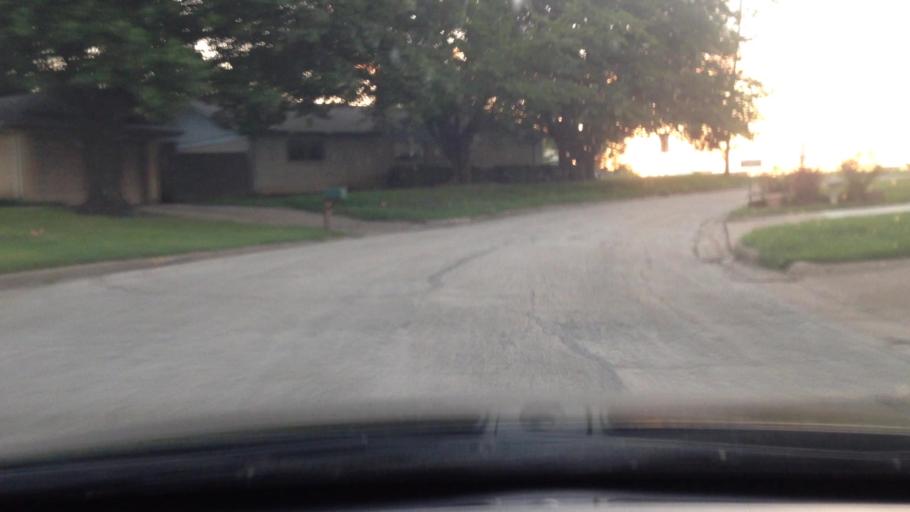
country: US
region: Texas
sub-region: Tarrant County
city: White Settlement
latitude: 32.7763
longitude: -97.4670
